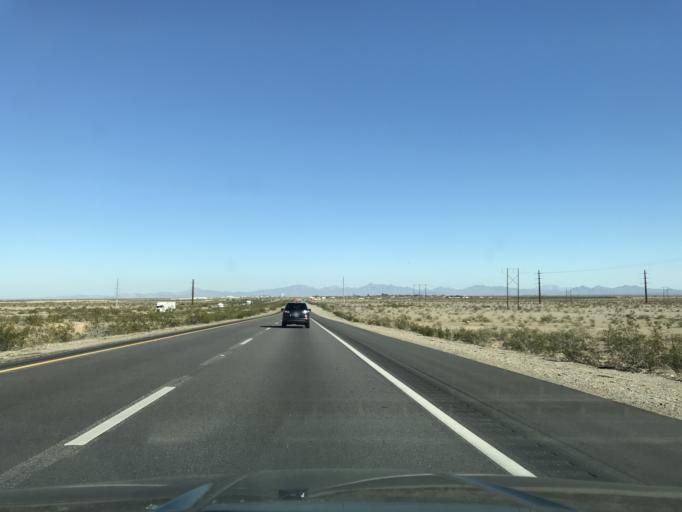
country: US
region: California
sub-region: Riverside County
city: Mesa Verde
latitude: 33.6087
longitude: -114.7601
